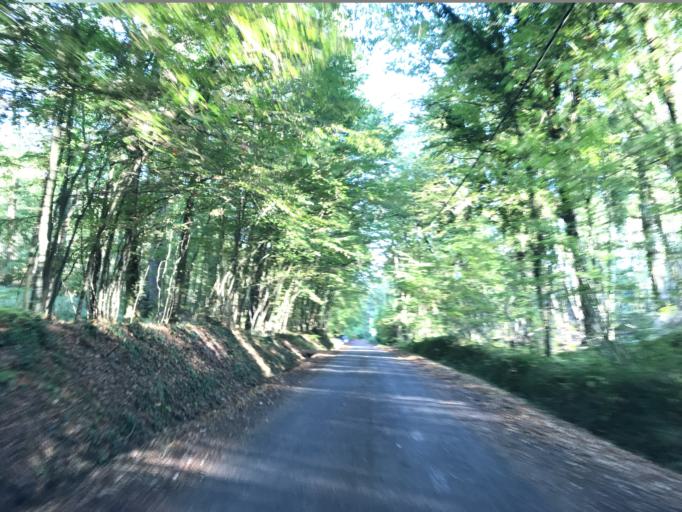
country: FR
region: Haute-Normandie
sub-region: Departement de l'Eure
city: Saint-Aubin-sur-Gaillon
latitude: 49.0739
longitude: 1.2717
